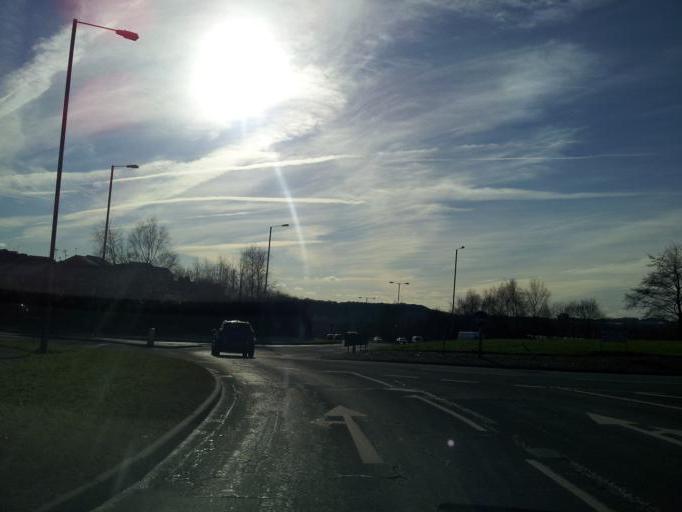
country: GB
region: England
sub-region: Staffordshire
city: Kidsgrove
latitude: 53.0661
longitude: -2.2211
